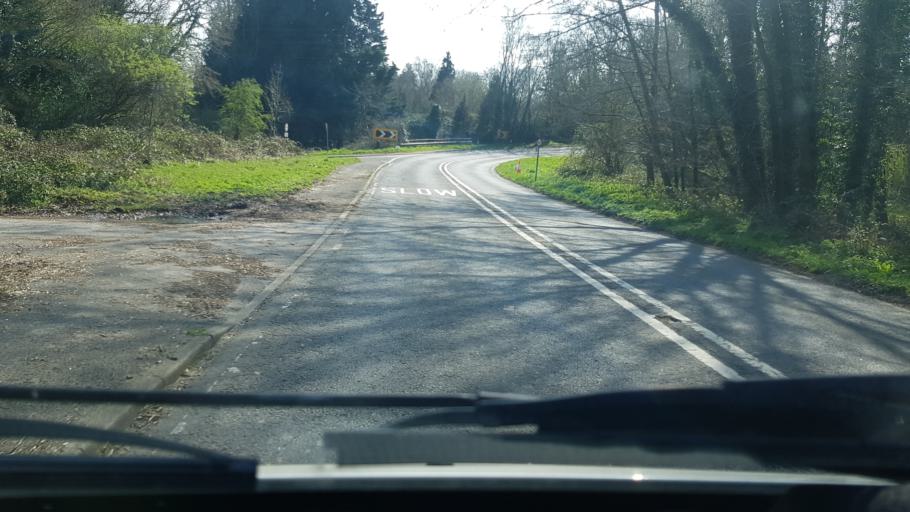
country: GB
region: England
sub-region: West Sussex
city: Fernhurst
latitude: 51.0392
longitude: -0.7243
